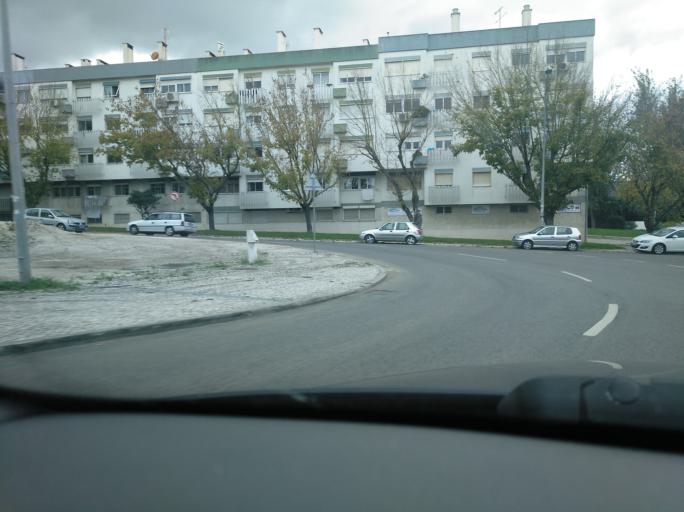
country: PT
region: Lisbon
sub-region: Amadora
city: Amadora
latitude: 38.7389
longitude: -9.2109
